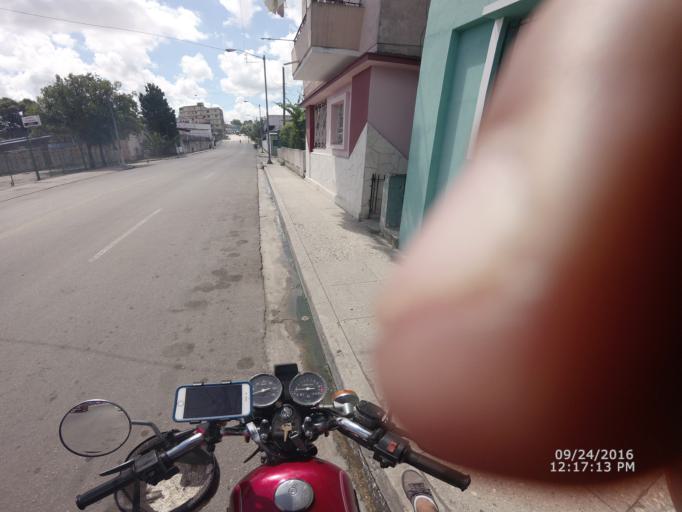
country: CU
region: La Habana
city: Diez de Octubre
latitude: 23.1048
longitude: -82.3511
